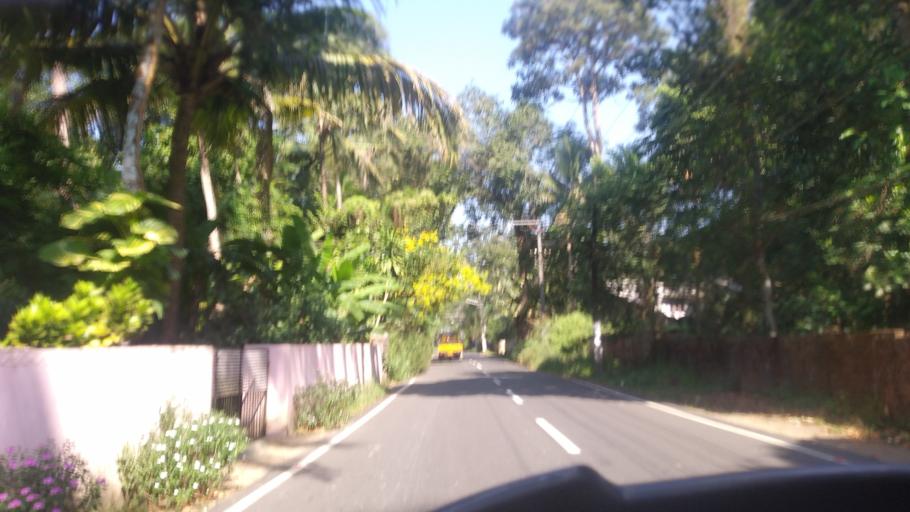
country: IN
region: Kerala
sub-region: Ernakulam
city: Elur
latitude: 10.1123
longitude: 76.2485
